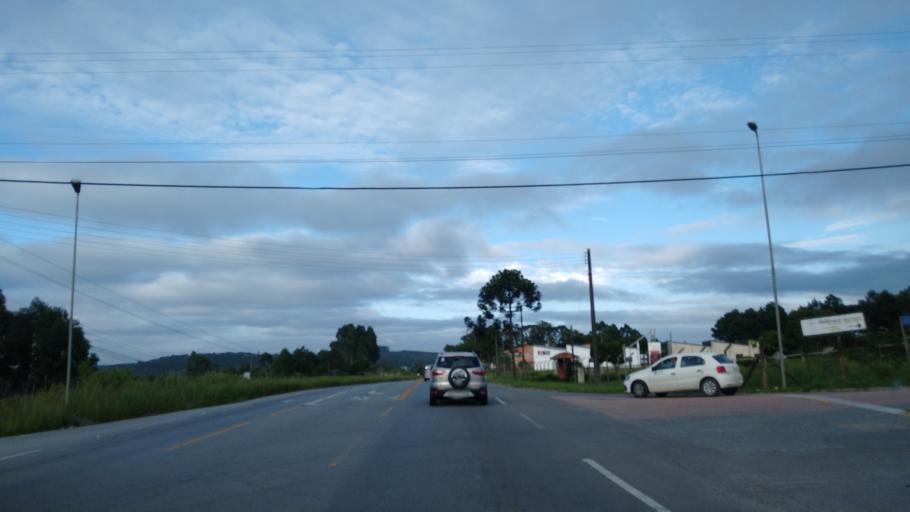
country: BR
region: Santa Catarina
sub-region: Sao Bento Do Sul
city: Sao Bento do Sul
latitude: -26.2451
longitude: -49.4428
